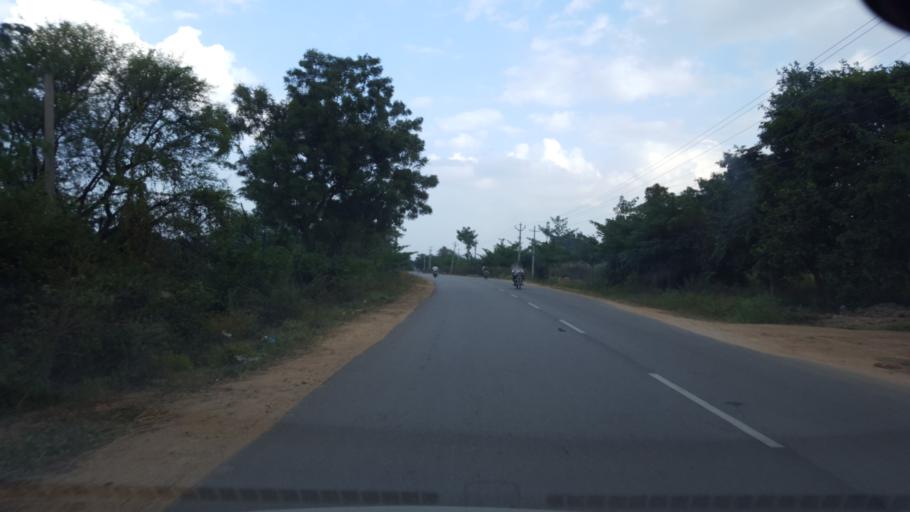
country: IN
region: Telangana
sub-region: Mahbubnagar
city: Mahbubnagar
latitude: 16.7592
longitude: 77.9616
